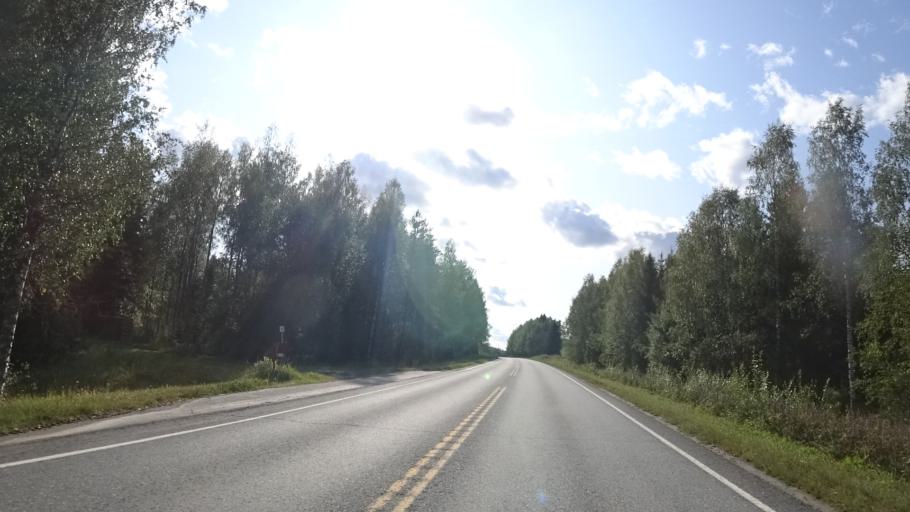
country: FI
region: North Karelia
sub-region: Keski-Karjala
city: Kitee
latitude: 62.0958
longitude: 30.0691
